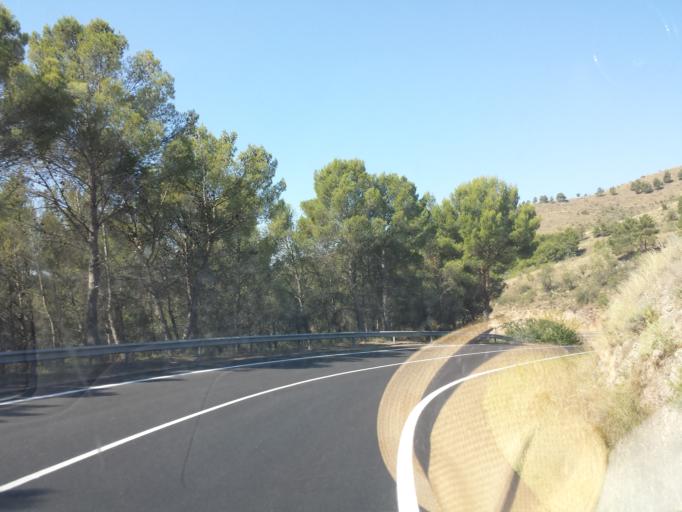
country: ES
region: Aragon
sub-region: Provincia de Zaragoza
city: Nuevalos
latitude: 41.2205
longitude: -1.7475
